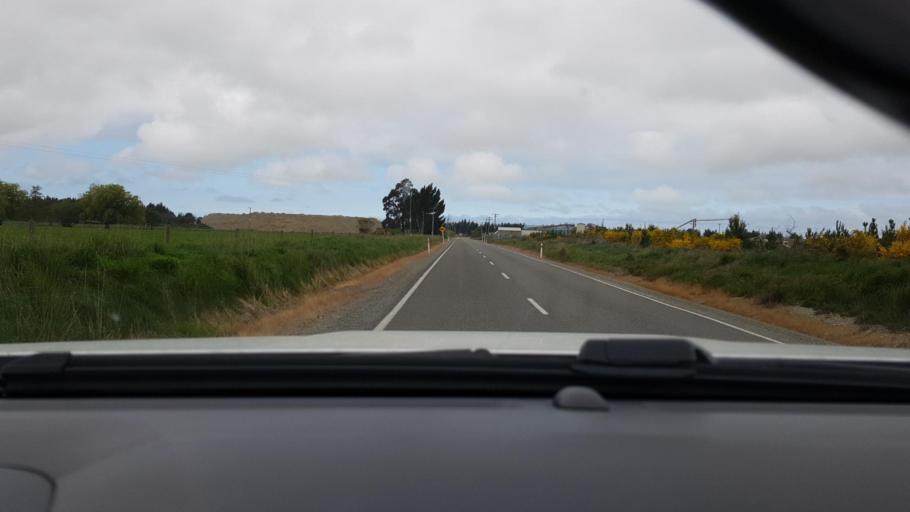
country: NZ
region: Otago
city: Oamaru
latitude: -44.9642
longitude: 171.0692
